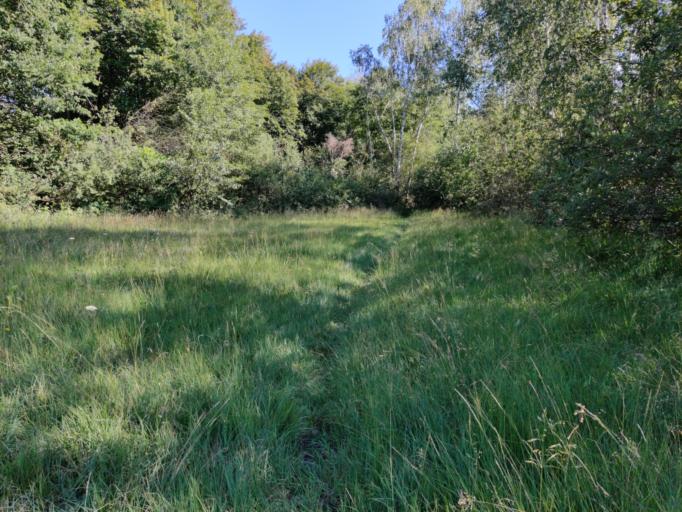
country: AT
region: Carinthia
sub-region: Klagenfurt am Woerthersee
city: Klagenfurt am Woerthersee
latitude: 46.6115
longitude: 14.2573
